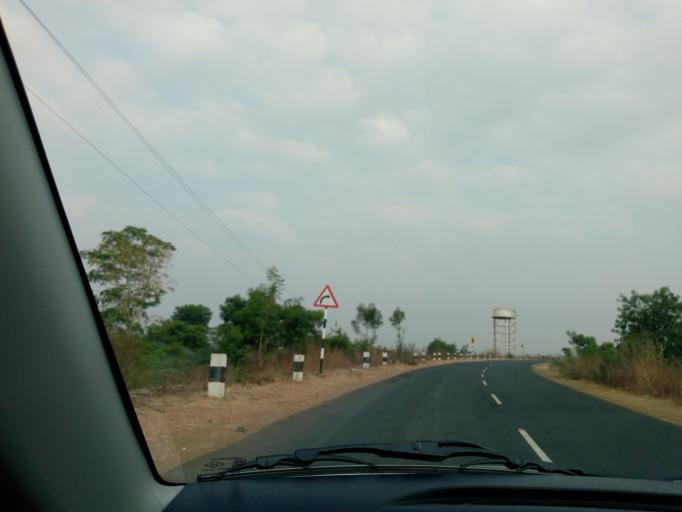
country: IN
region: Andhra Pradesh
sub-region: Prakasam
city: Diguvametta
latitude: 15.3739
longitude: 78.8721
